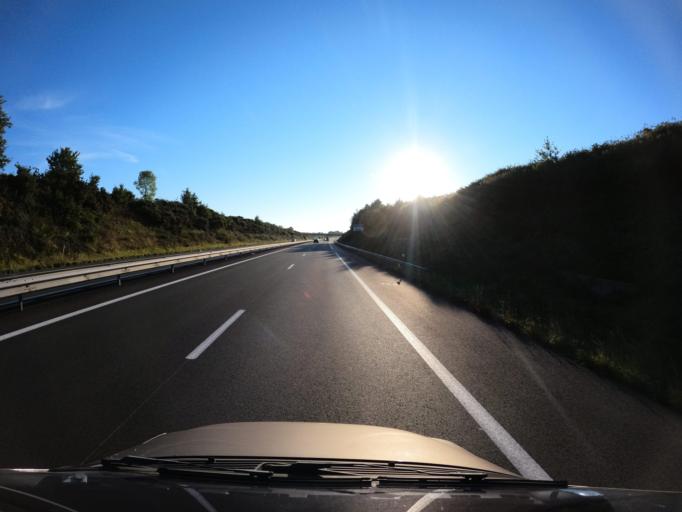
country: FR
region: Pays de la Loire
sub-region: Departement de la Vendee
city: Saint-Fulgent
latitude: 46.8188
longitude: -1.1835
